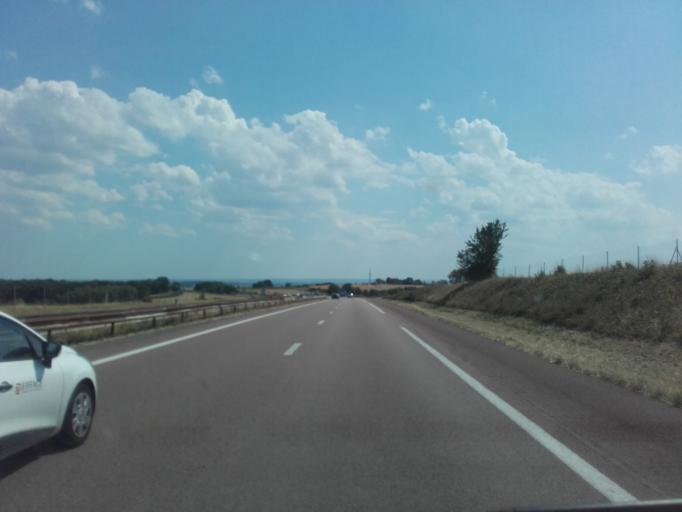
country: FR
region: Bourgogne
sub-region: Departement de l'Yonne
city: Avallon
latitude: 47.5661
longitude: 3.9407
